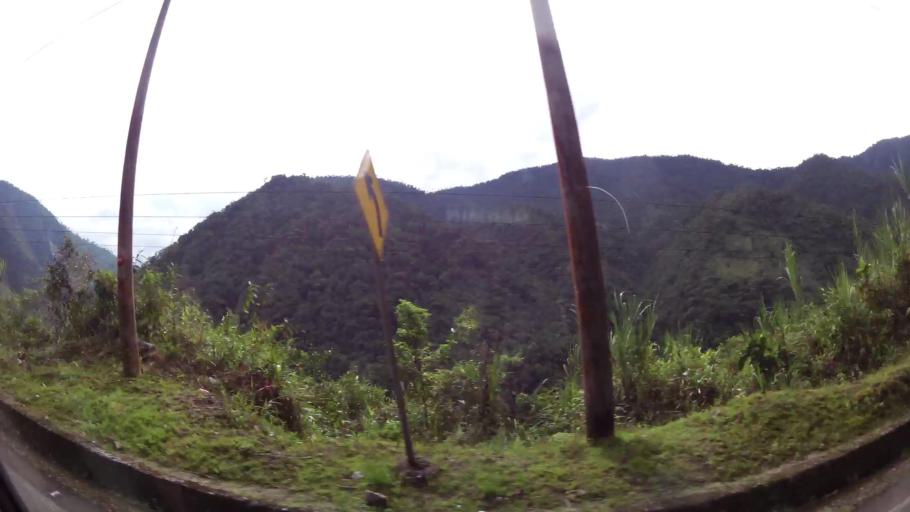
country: EC
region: Pastaza
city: Puyo
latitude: -1.4442
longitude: -78.1787
